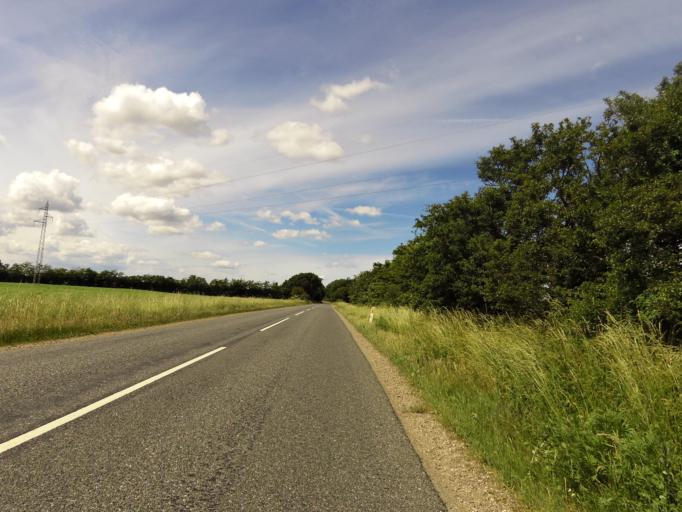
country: DK
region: South Denmark
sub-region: Esbjerg Kommune
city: Ribe
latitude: 55.2761
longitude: 8.7999
